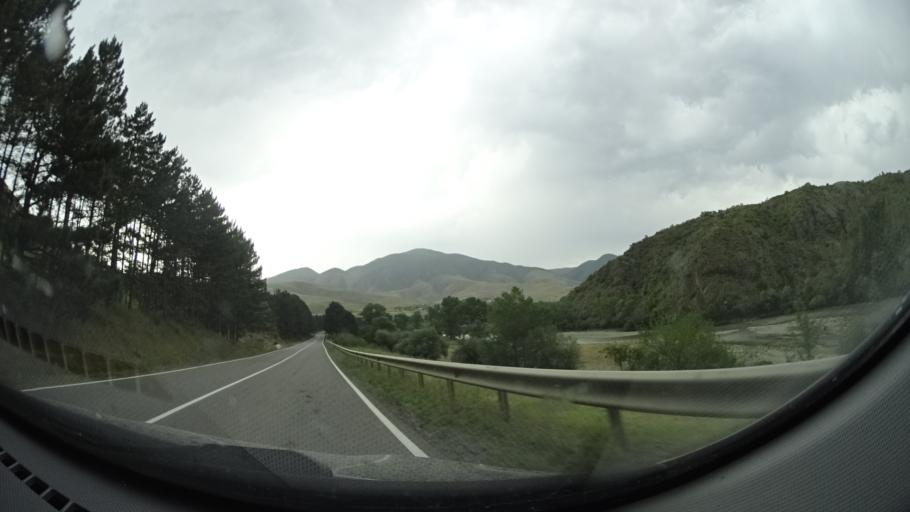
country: GE
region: Samtskhe-Javakheti
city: Akhaltsikhe
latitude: 41.6848
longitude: 43.0684
